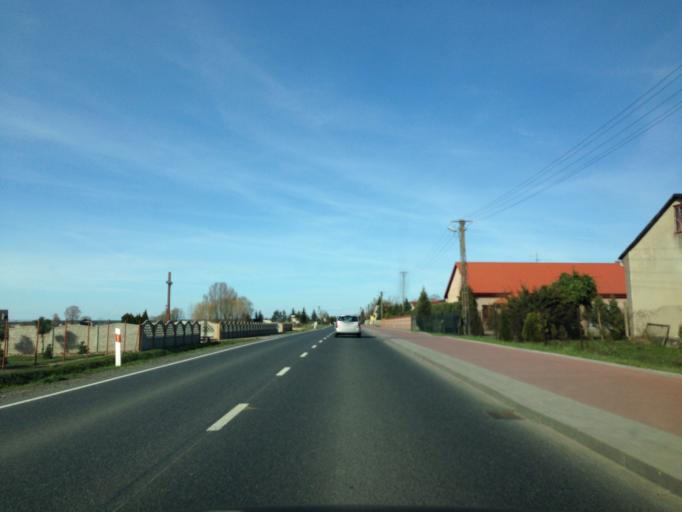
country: PL
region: Lodz Voivodeship
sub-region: Powiat poddebicki
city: Wartkowice
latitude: 51.9787
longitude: 19.0254
